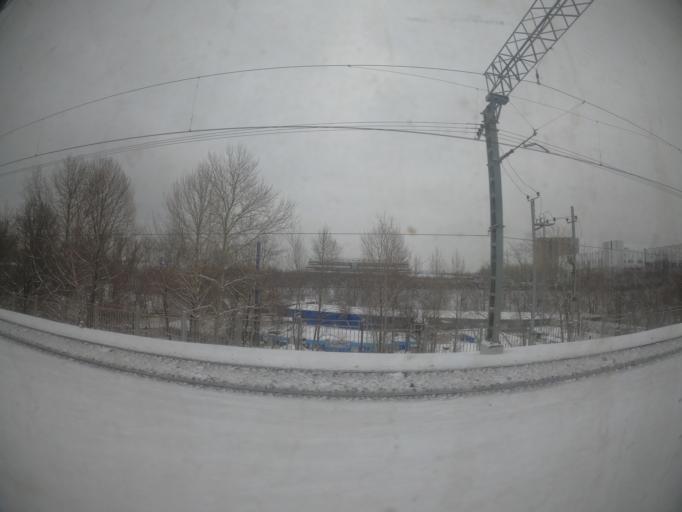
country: RU
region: Moscow
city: Kotlovka
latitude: 55.6875
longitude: 37.6188
